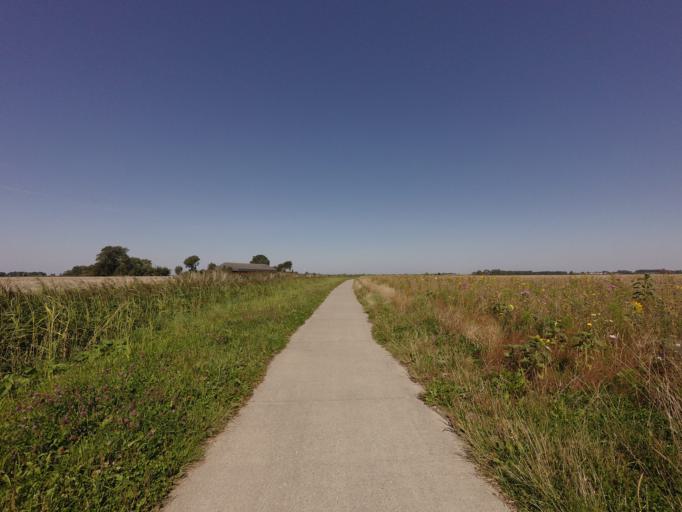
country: NL
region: Friesland
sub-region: Gemeente Dongeradeel
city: Anjum
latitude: 53.3897
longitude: 6.0657
